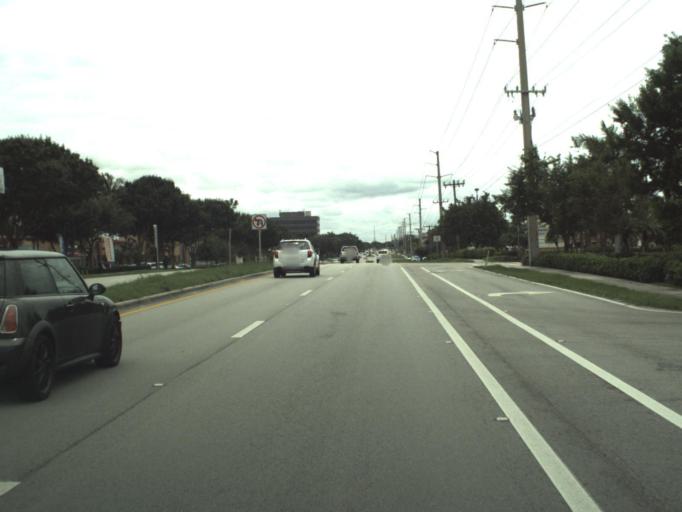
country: US
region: Florida
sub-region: Palm Beach County
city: Juno Beach
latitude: 26.8552
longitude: -80.0576
